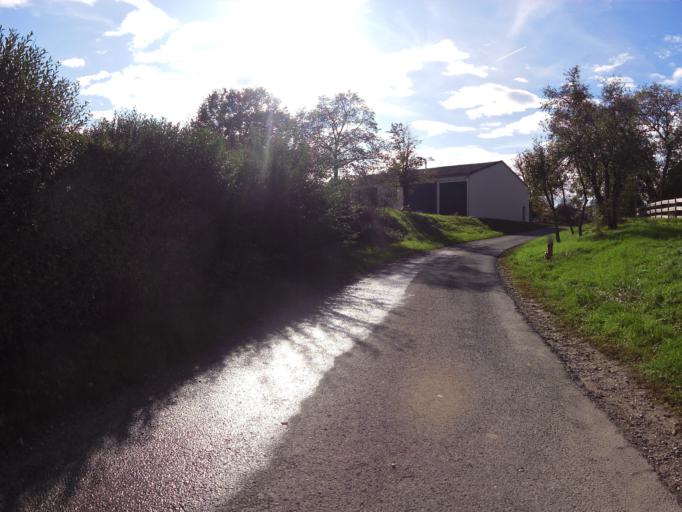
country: DE
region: Bavaria
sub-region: Regierungsbezirk Unterfranken
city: Biebelried
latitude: 49.7287
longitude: 10.0910
